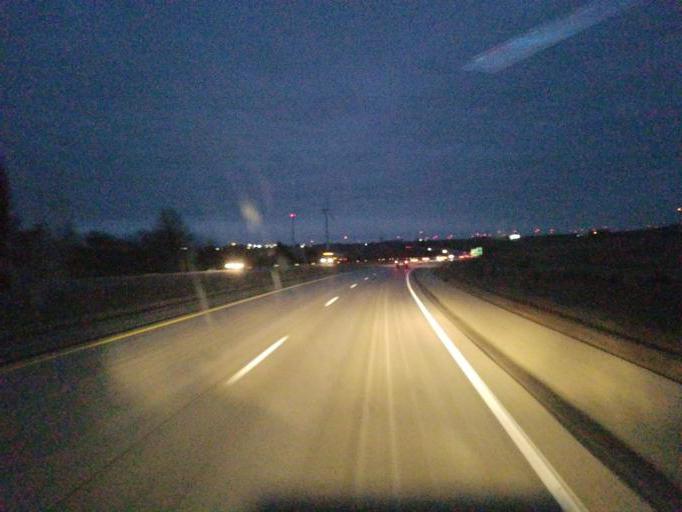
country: US
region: Iowa
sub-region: Guthrie County
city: Guthrie Center
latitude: 41.4966
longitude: -94.6862
